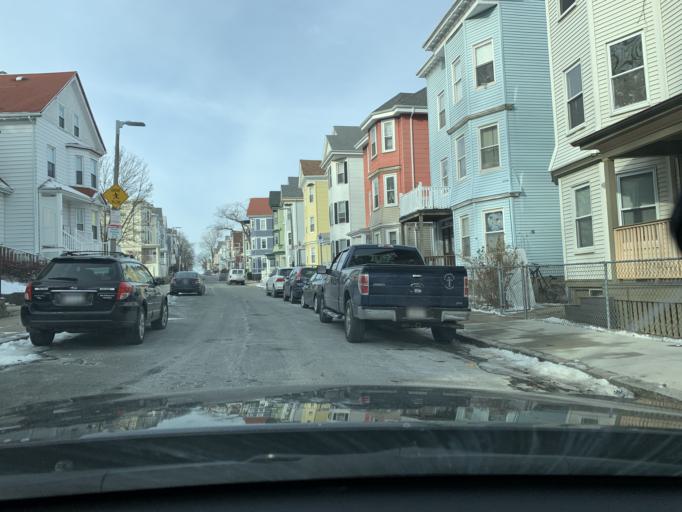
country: US
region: Massachusetts
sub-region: Norfolk County
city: Brookline
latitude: 42.3300
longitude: -71.1007
